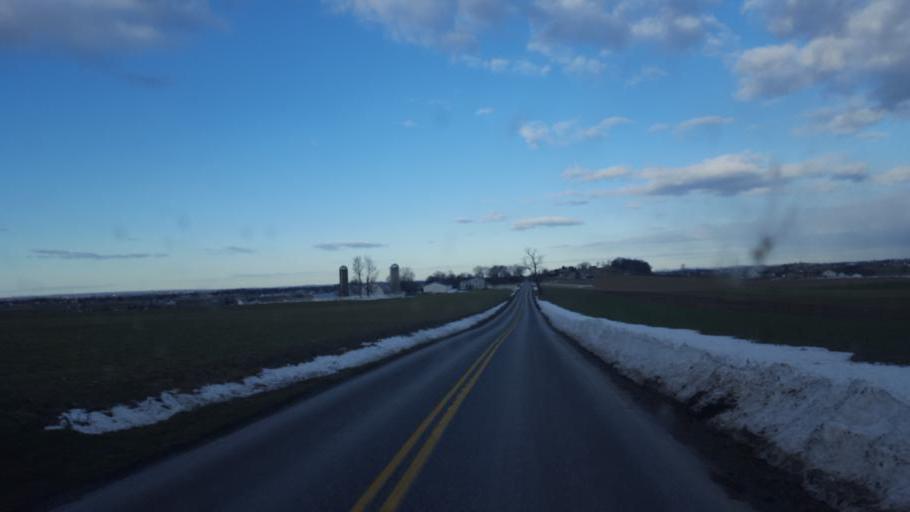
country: US
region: Pennsylvania
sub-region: Lancaster County
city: Intercourse
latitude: 40.0567
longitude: -76.0750
